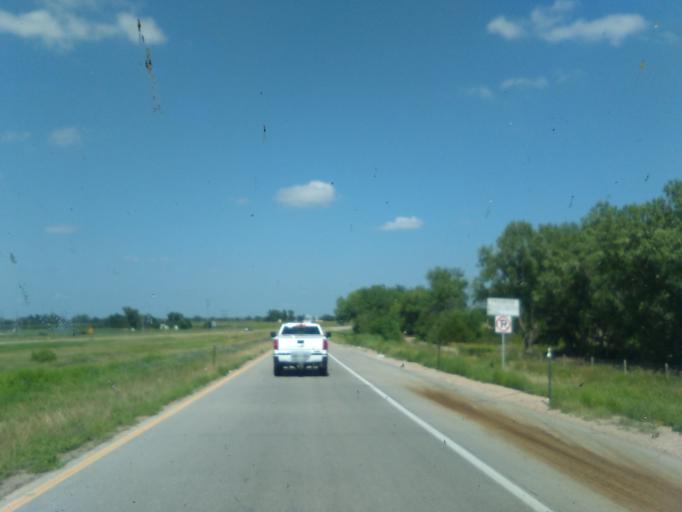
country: US
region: Nebraska
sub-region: Phelps County
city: Holdrege
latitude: 40.6887
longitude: -99.3790
